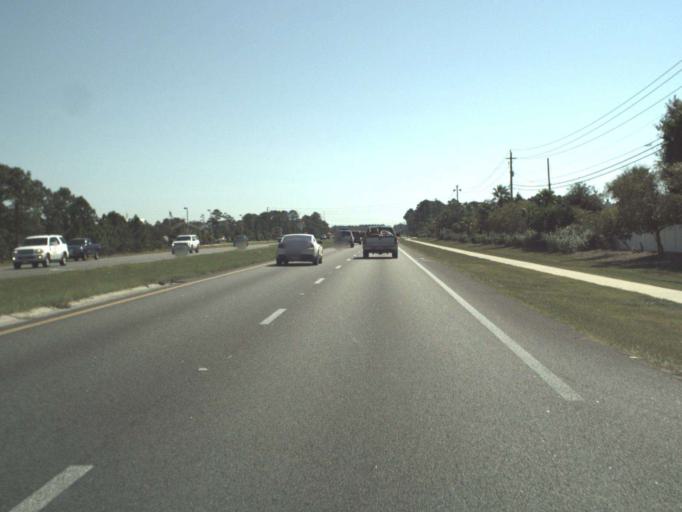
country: US
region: Florida
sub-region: Bay County
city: Panama City Beach
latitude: 30.2157
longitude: -85.8577
